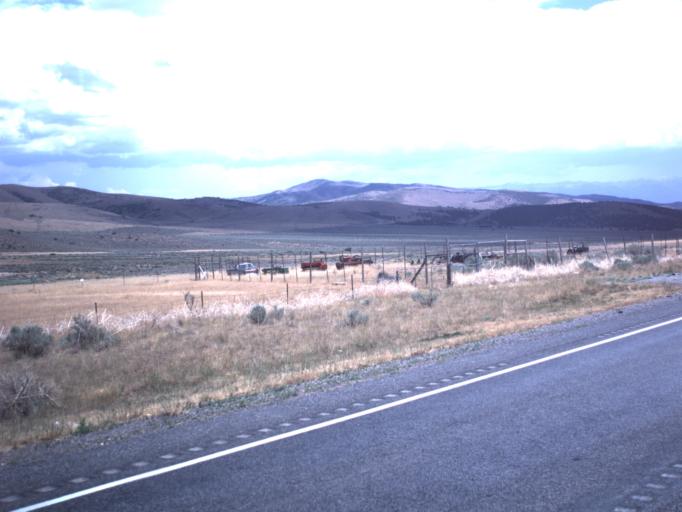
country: US
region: Utah
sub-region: Sanpete County
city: Fountain Green
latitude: 39.6630
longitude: -111.6570
